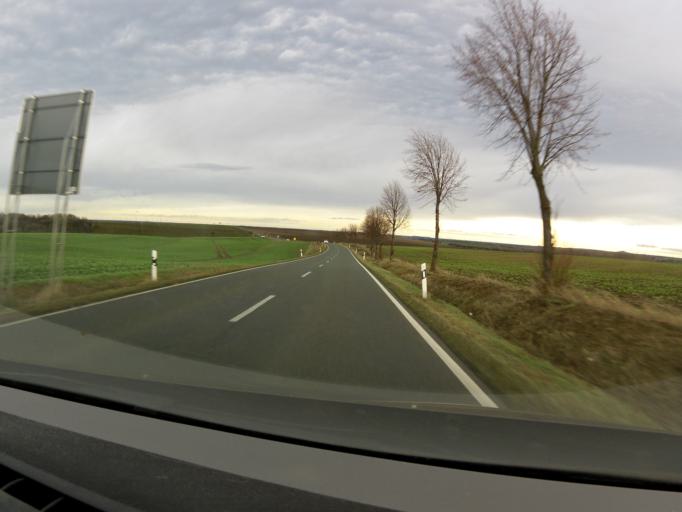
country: DE
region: Saxony-Anhalt
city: Belleben
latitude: 51.6890
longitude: 11.6397
